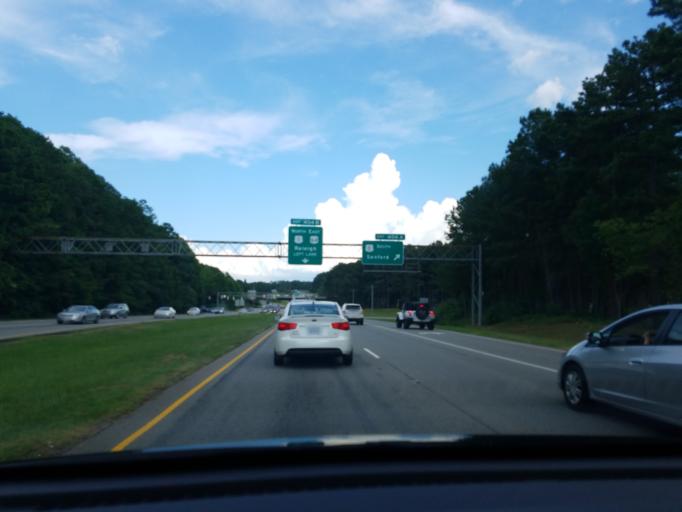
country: US
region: North Carolina
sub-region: Wake County
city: Apex
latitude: 35.7383
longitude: -78.7967
